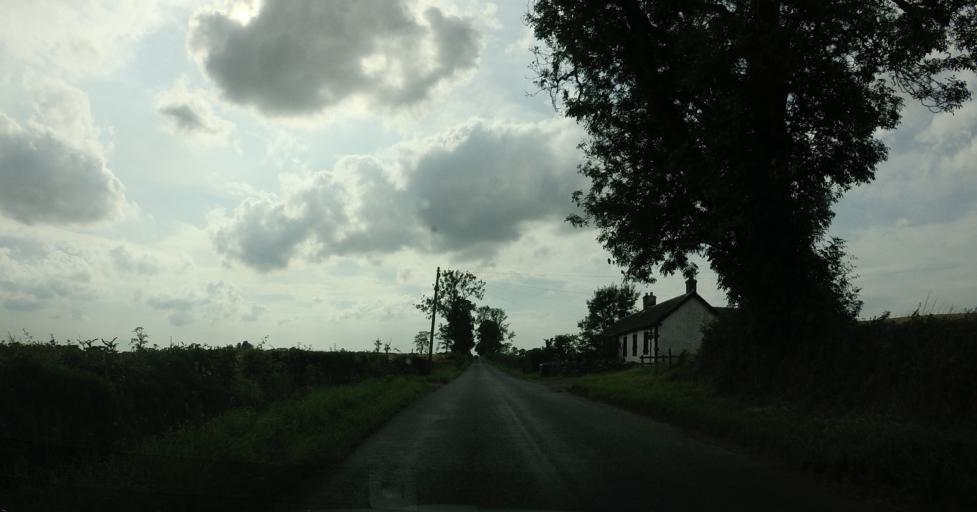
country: GB
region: Scotland
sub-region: Perth and Kinross
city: Methven
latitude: 56.3770
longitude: -3.6641
